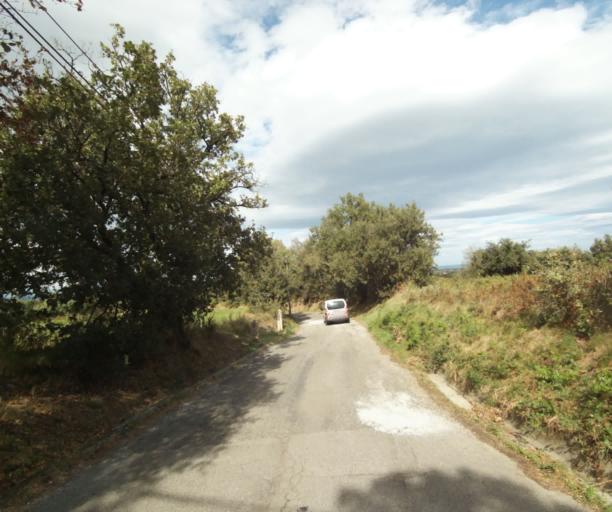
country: FR
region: Languedoc-Roussillon
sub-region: Departement des Pyrenees-Orientales
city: Sorede
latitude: 42.5273
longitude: 2.9842
